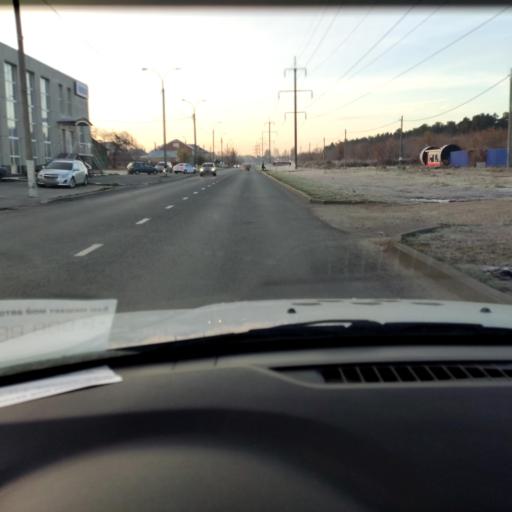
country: RU
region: Samara
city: Tol'yatti
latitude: 53.5207
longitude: 49.3957
